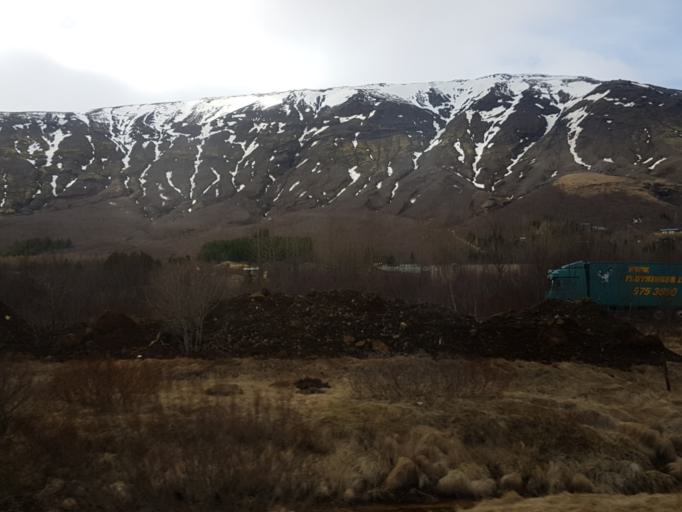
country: IS
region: South
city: Selfoss
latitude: 64.2301
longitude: -20.7163
